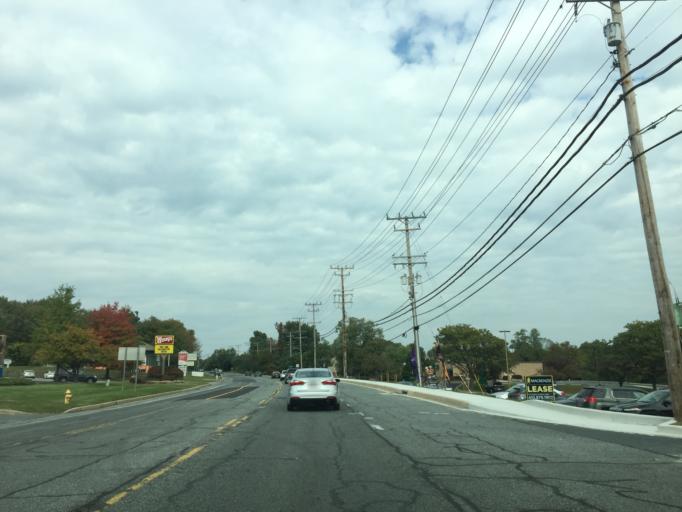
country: US
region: Maryland
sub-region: Harford County
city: Bel Air South
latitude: 39.4788
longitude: -76.3103
